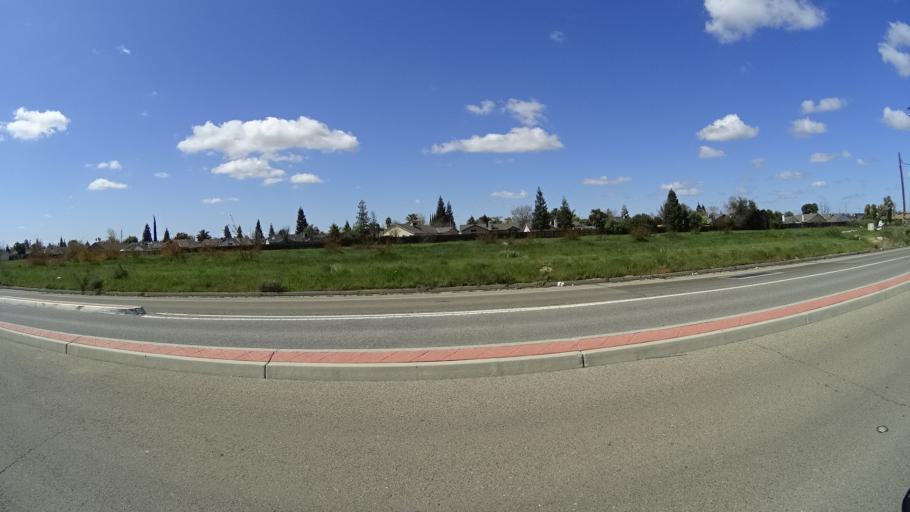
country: US
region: California
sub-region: Fresno County
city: West Park
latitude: 36.7624
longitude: -119.8890
